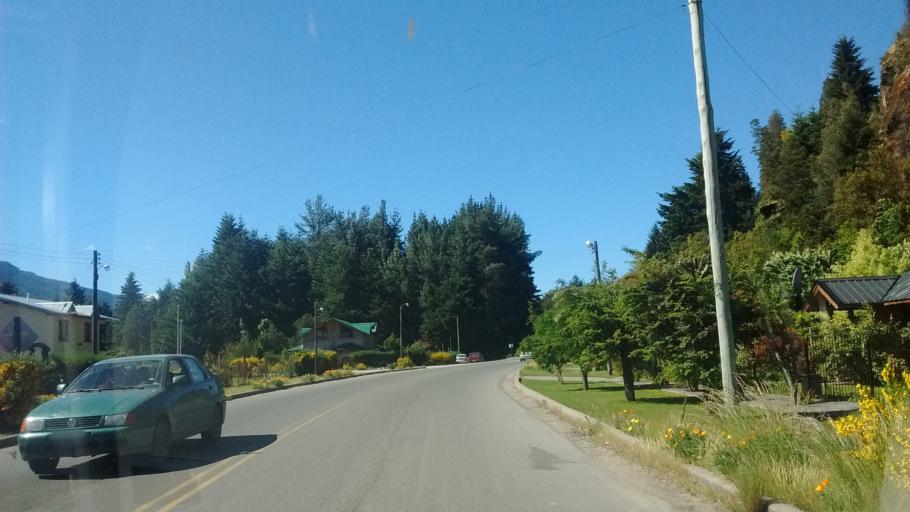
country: AR
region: Chubut
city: Lago Puelo
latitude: -42.0522
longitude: -71.5960
